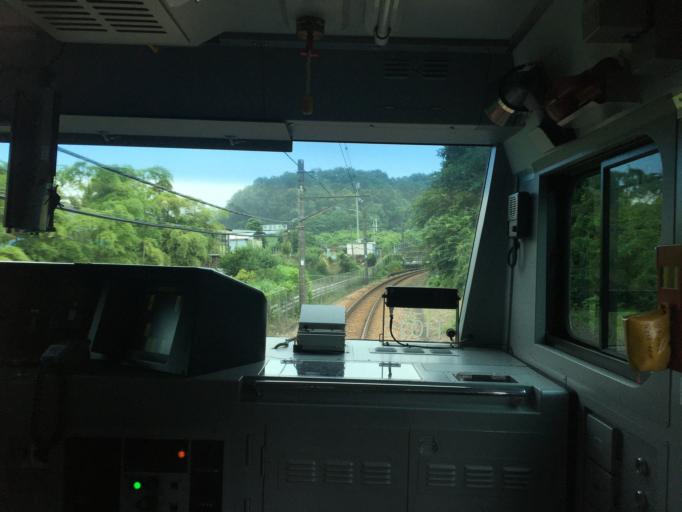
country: JP
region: Tokyo
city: Hachioji
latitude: 35.6208
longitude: 139.3331
